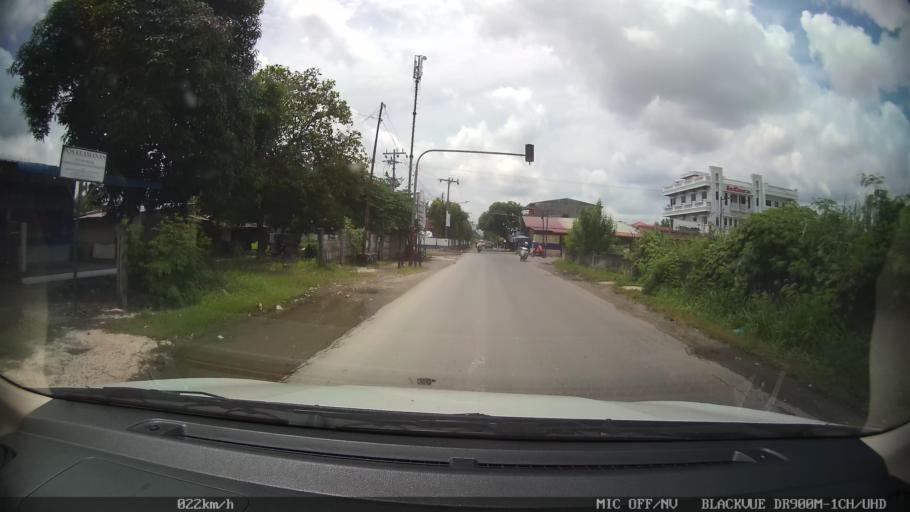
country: ID
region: North Sumatra
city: Medan
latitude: 3.6062
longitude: 98.7288
